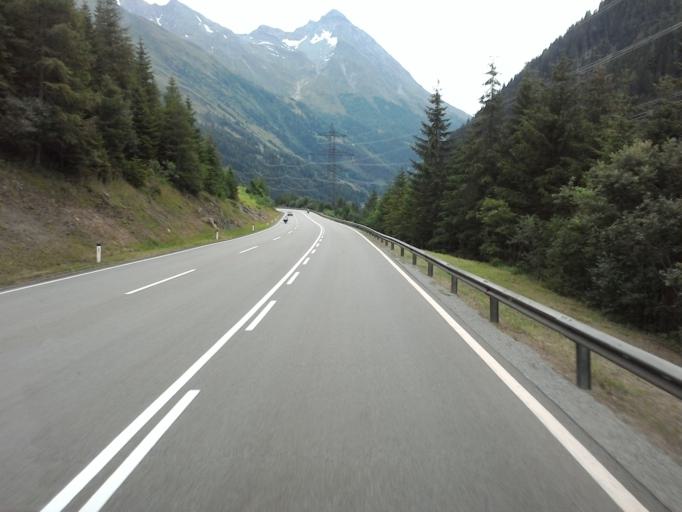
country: AT
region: Tyrol
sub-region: Politischer Bezirk Lienz
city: Matrei in Osttirol
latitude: 47.0953
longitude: 12.5187
